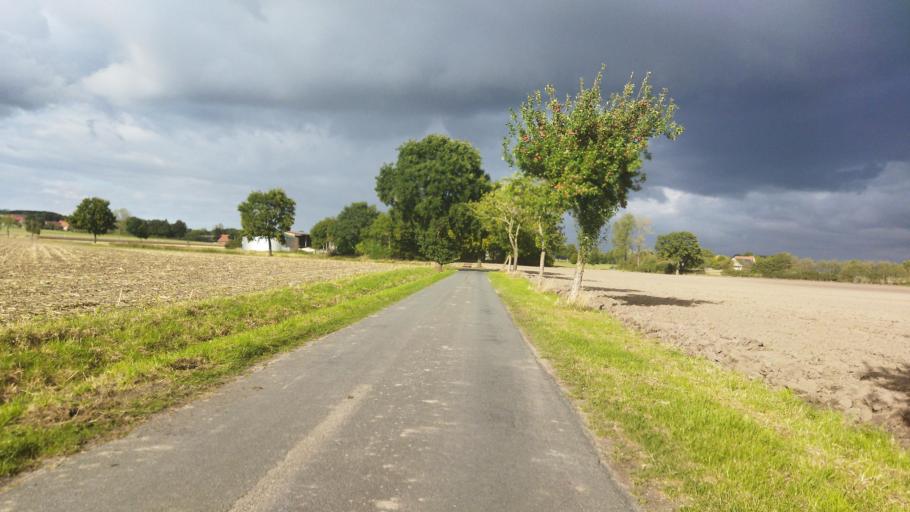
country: DE
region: North Rhine-Westphalia
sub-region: Regierungsbezirk Munster
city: Dulmen
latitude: 51.9031
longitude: 7.2620
